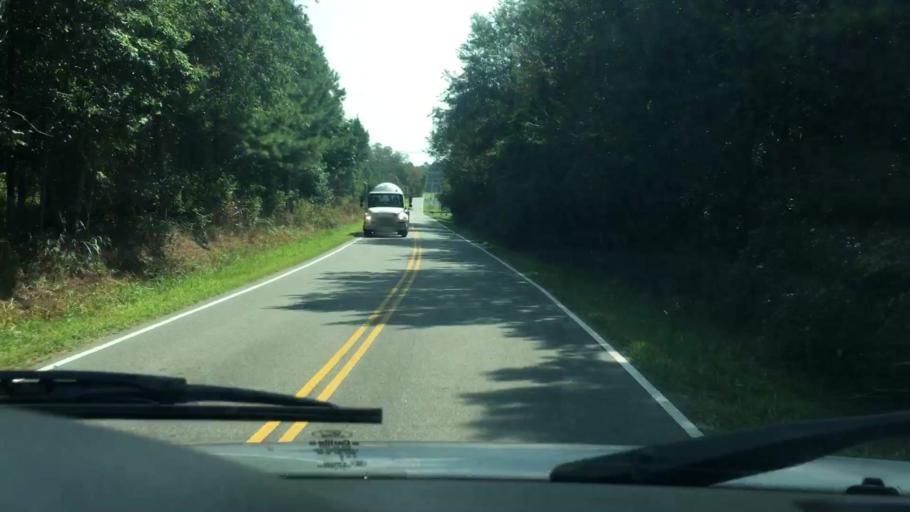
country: US
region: North Carolina
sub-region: Gaston County
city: Davidson
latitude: 35.4833
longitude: -80.8181
